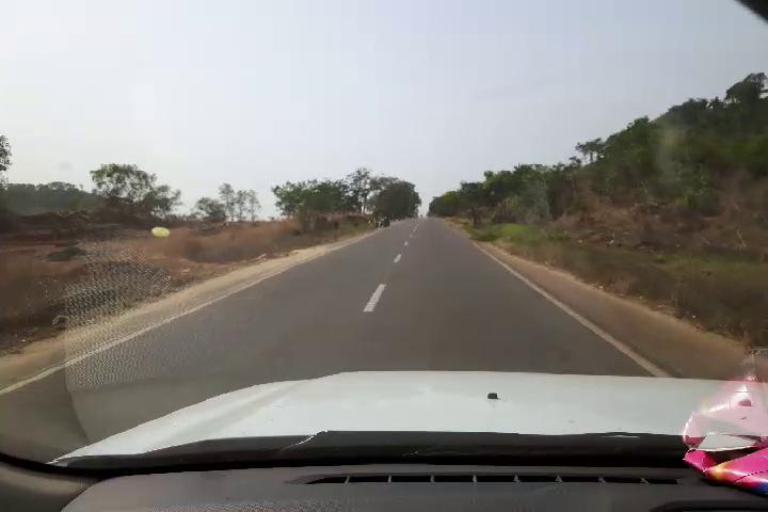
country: SL
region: Western Area
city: Waterloo
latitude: 8.2100
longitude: -13.1341
